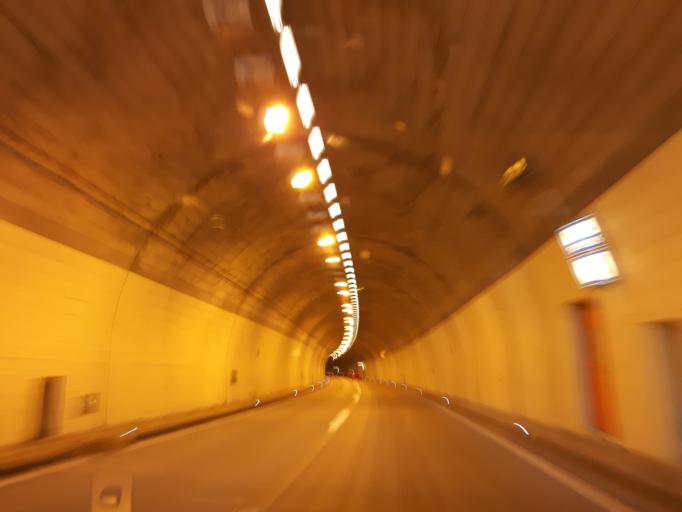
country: CH
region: Saint Gallen
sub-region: Wahlkreis Sarganserland
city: Quarten
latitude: 47.1109
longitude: 9.2212
